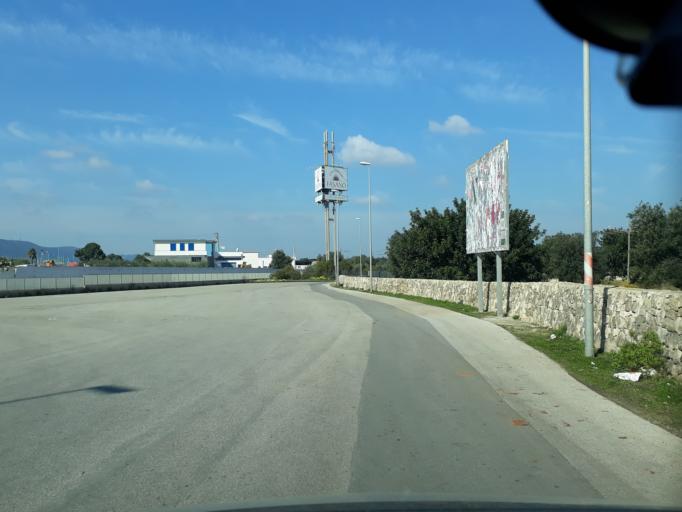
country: IT
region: Apulia
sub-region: Provincia di Brindisi
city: Fasano
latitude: 40.8259
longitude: 17.3843
